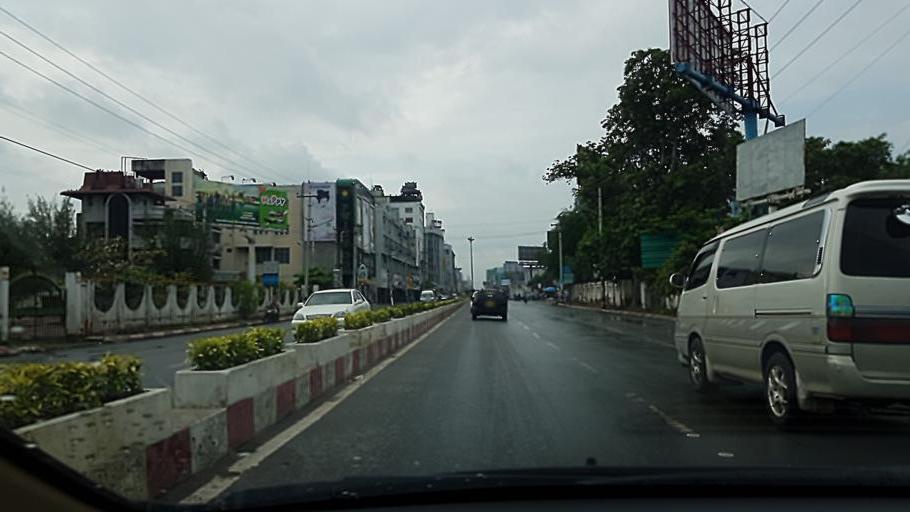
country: MM
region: Mandalay
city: Mandalay
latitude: 21.9792
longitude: 96.0870
